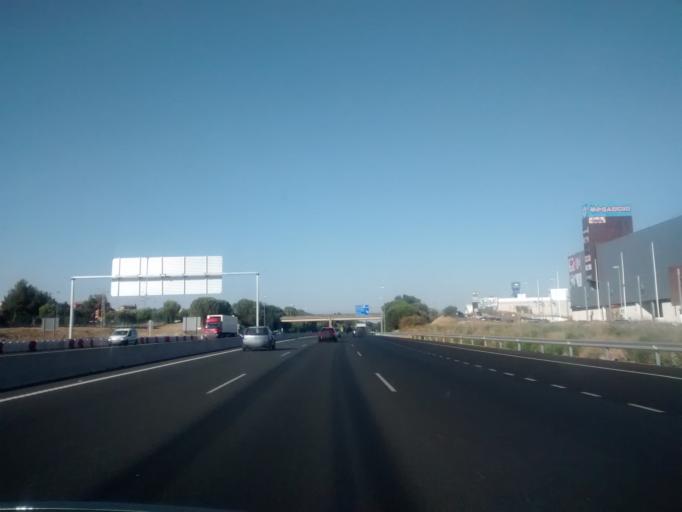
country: ES
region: Andalusia
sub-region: Provincia de Sevilla
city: Bormujos
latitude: 37.3799
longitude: -6.0739
